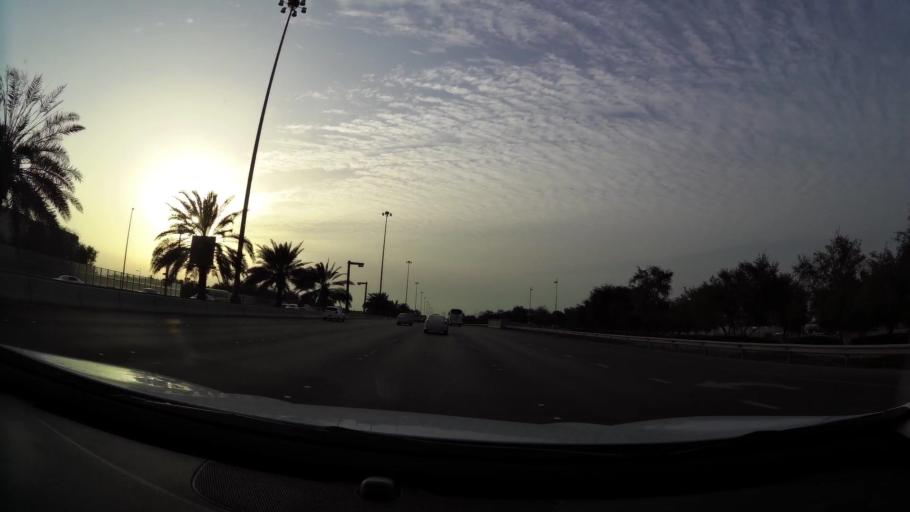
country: AE
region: Abu Dhabi
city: Abu Dhabi
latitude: 24.3988
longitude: 54.5034
